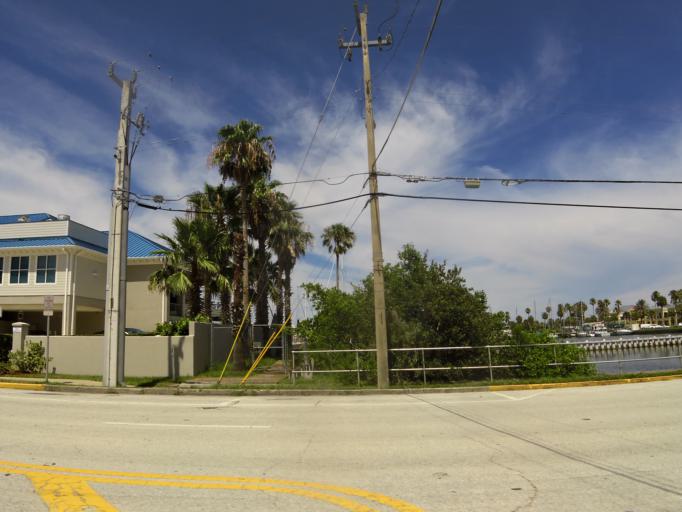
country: US
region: Florida
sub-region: Volusia County
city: Daytona Beach
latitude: 29.2071
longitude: -81.0171
